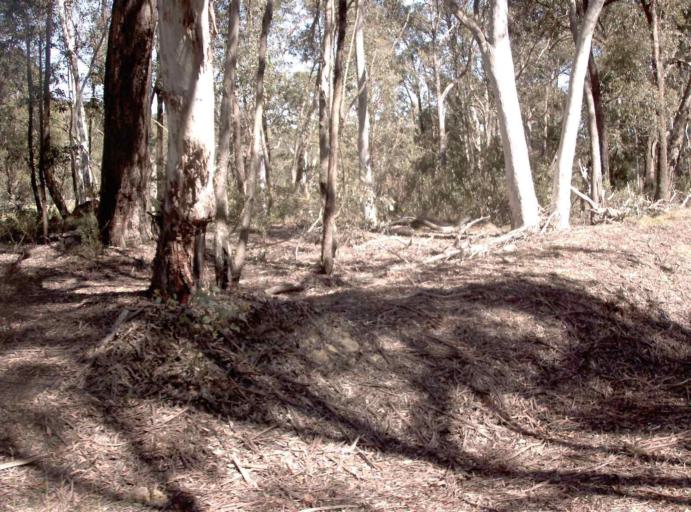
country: AU
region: New South Wales
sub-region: Bombala
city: Bombala
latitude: -37.1430
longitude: 148.7234
